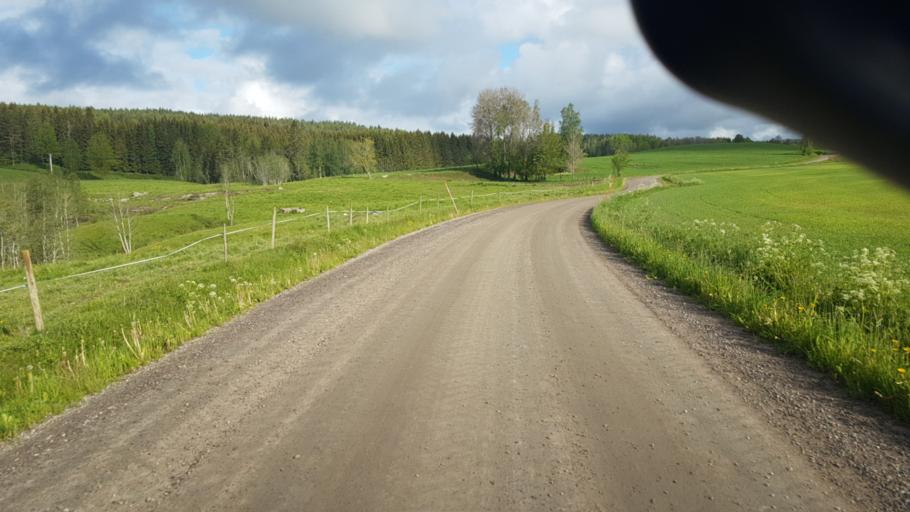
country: SE
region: Vaermland
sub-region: Eda Kommun
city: Amotfors
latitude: 59.7189
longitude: 12.1456
